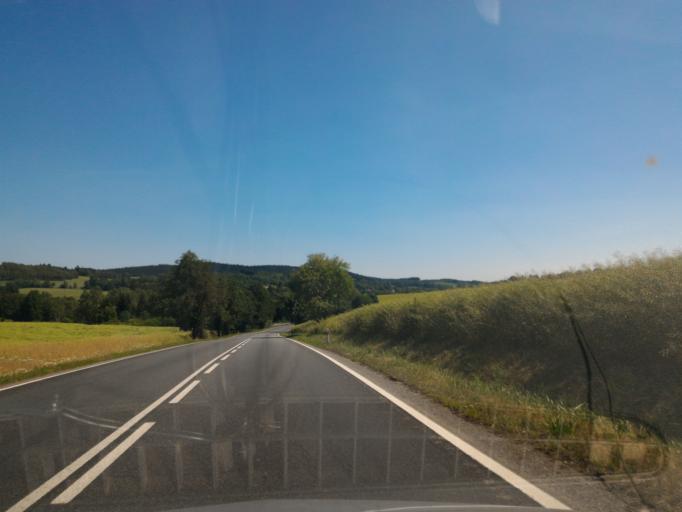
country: CZ
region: Vysocina
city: Dolni Cerekev
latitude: 49.3439
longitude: 15.4839
